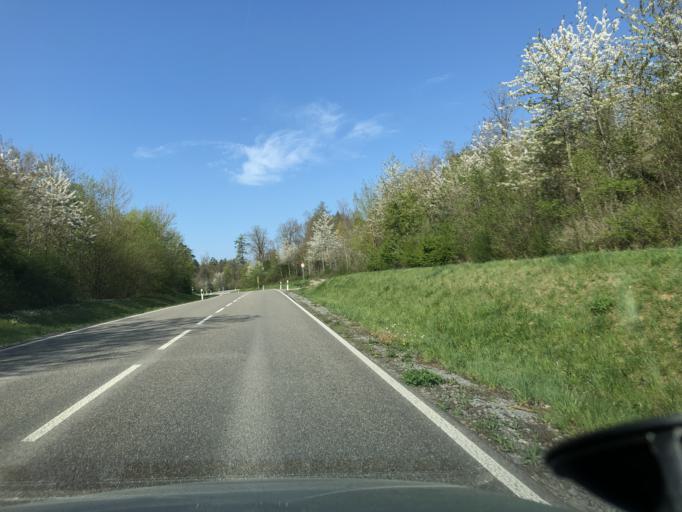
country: DE
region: Baden-Wuerttemberg
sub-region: Karlsruhe Region
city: Heimsheim
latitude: 48.8163
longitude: 8.9034
